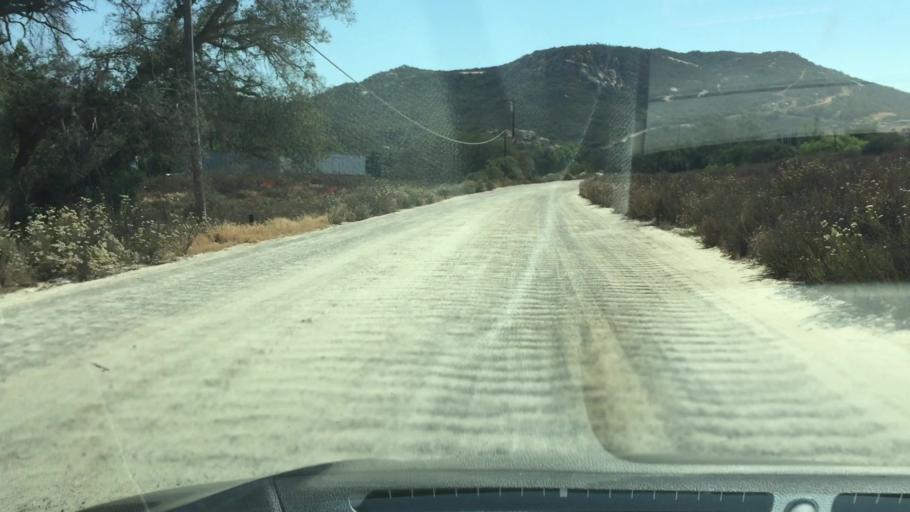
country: US
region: California
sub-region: San Diego County
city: Alpine
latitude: 32.7527
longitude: -116.7576
